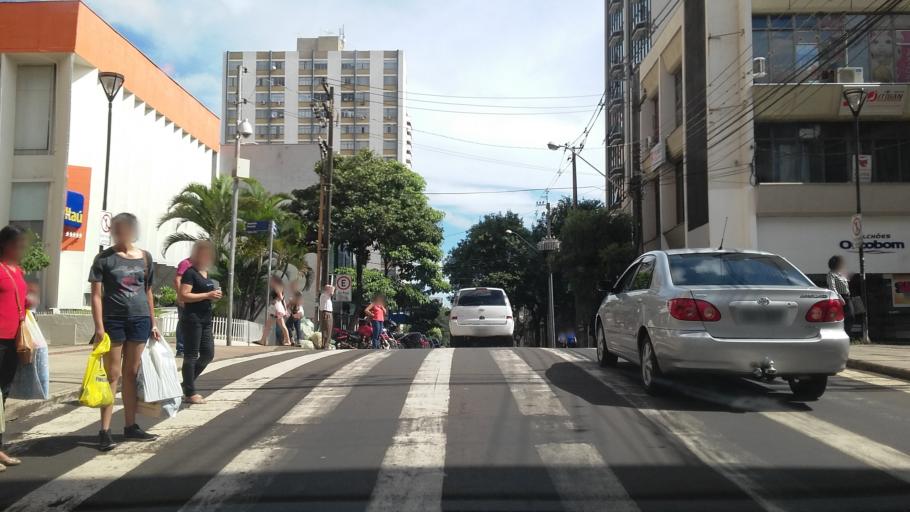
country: BR
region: Parana
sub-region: Londrina
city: Londrina
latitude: -23.3107
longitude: -51.1628
